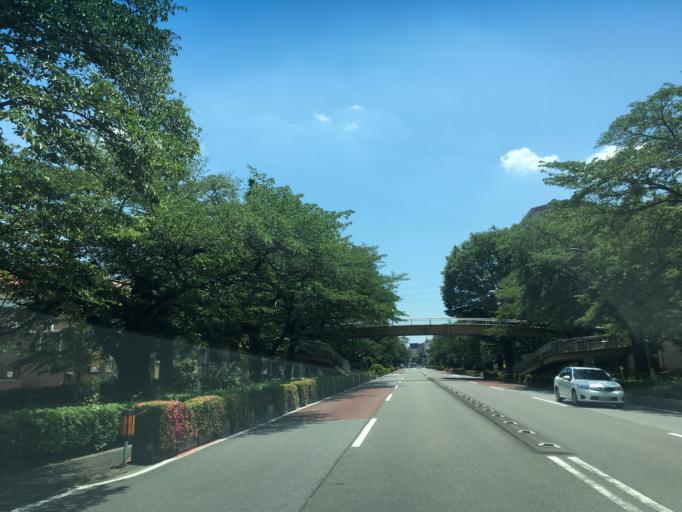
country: JP
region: Tokyo
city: Kokubunji
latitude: 35.6892
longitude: 139.4471
